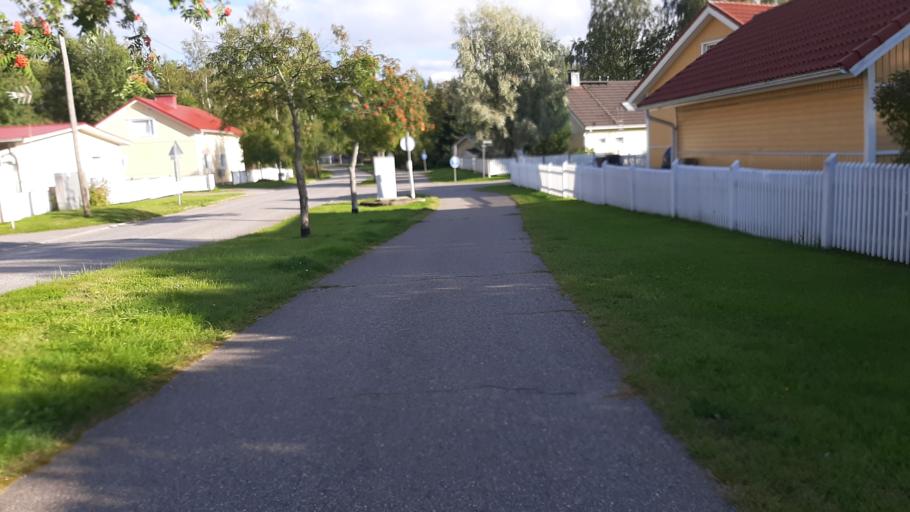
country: FI
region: North Karelia
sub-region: Joensuu
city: Joensuu
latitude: 62.6191
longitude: 29.7855
